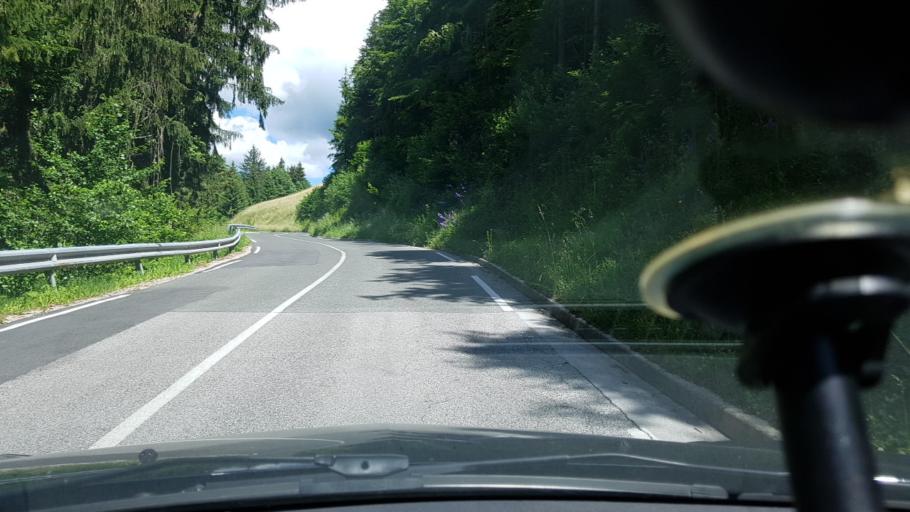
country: SI
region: Zrece
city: Zrece
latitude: 46.3953
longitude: 15.3730
